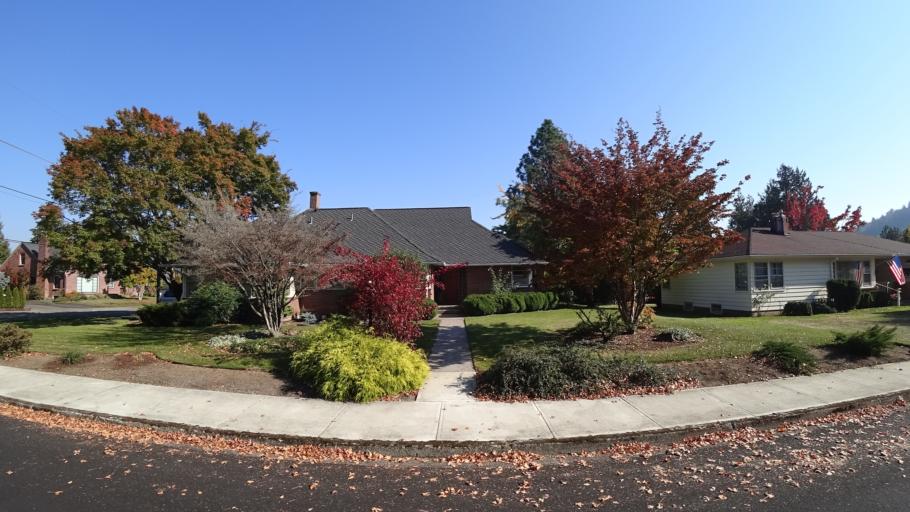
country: US
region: Oregon
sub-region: Multnomah County
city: Gresham
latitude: 45.4986
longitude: -122.4414
